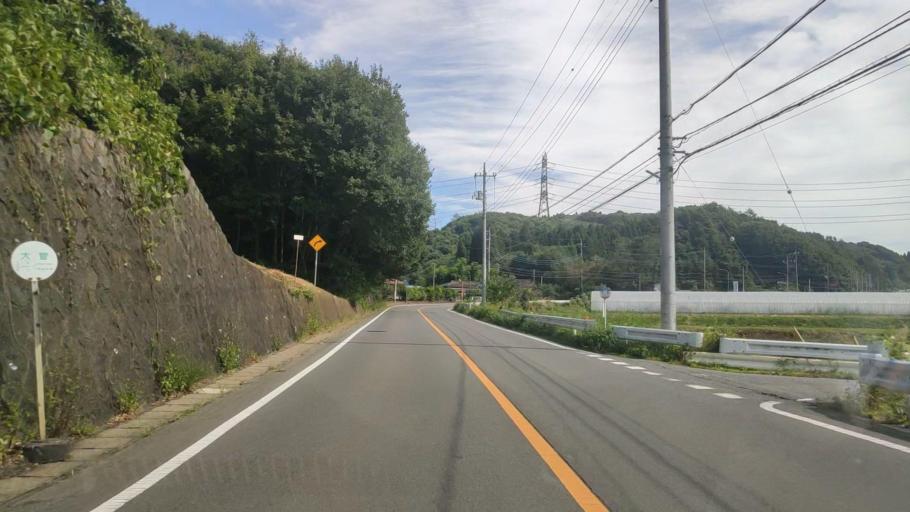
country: JP
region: Gunma
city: Numata
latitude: 36.6286
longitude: 138.9743
